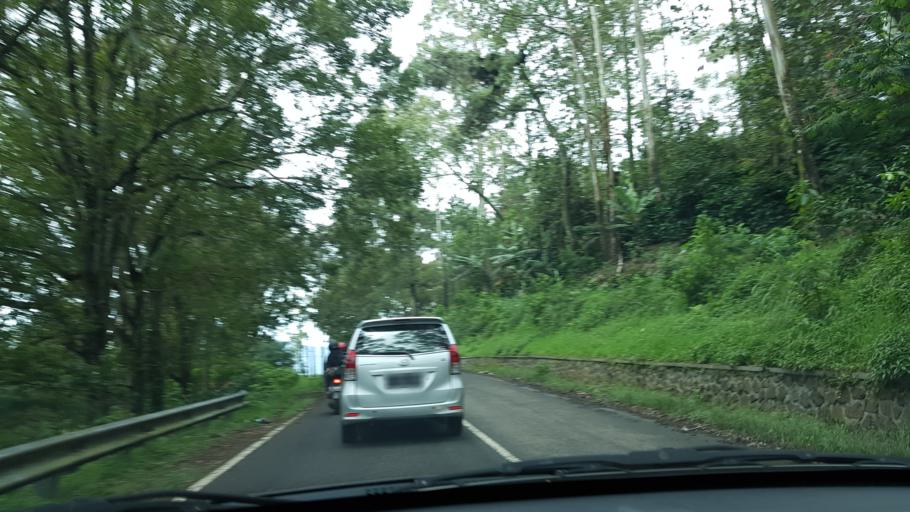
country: ID
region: West Java
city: Banjar
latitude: -7.1328
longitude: 107.4115
